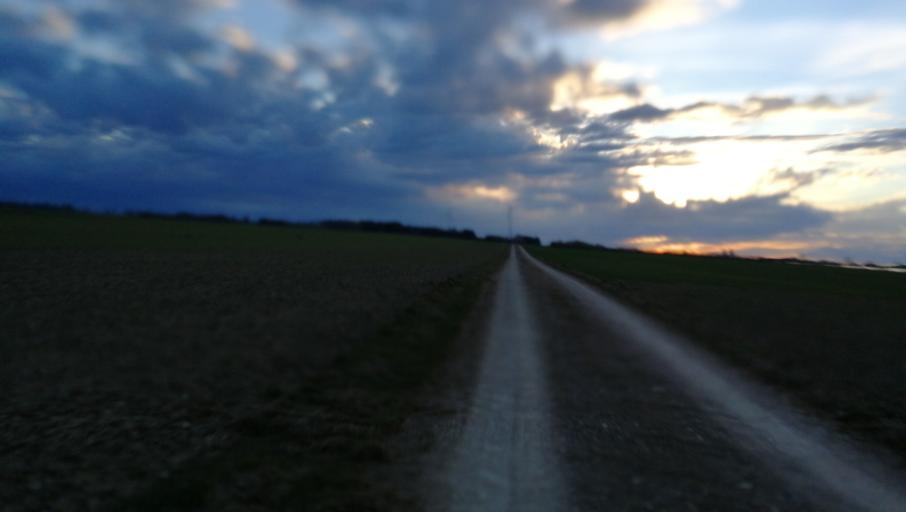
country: DE
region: Bavaria
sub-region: Upper Bavaria
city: Fuerstenfeldbruck
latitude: 48.2066
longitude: 11.2259
